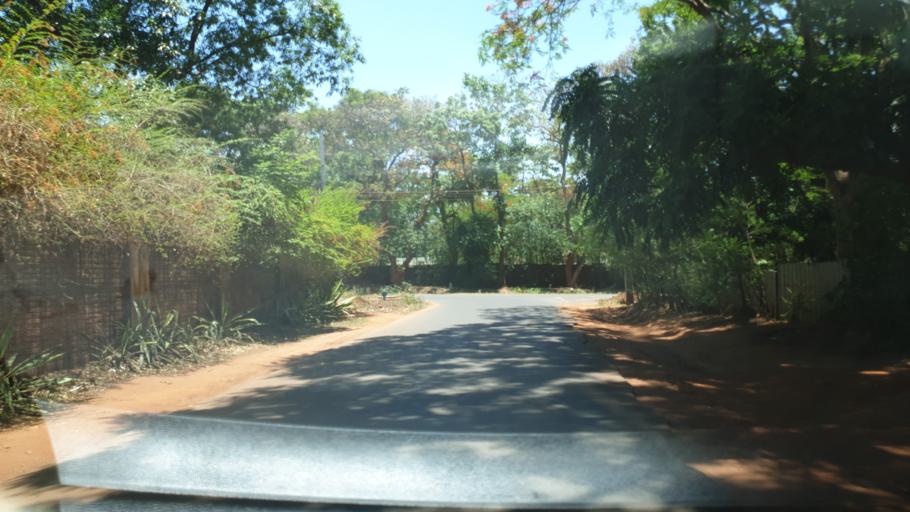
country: MW
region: Central Region
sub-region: Lilongwe District
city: Lilongwe
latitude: -13.9856
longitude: 33.7562
